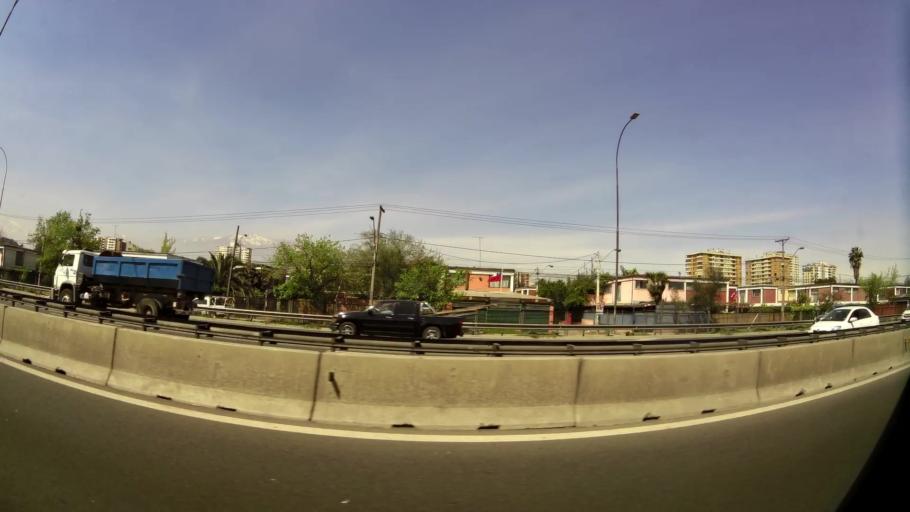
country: CL
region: Santiago Metropolitan
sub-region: Provincia de Santiago
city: Santiago
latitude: -33.4874
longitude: -70.6602
